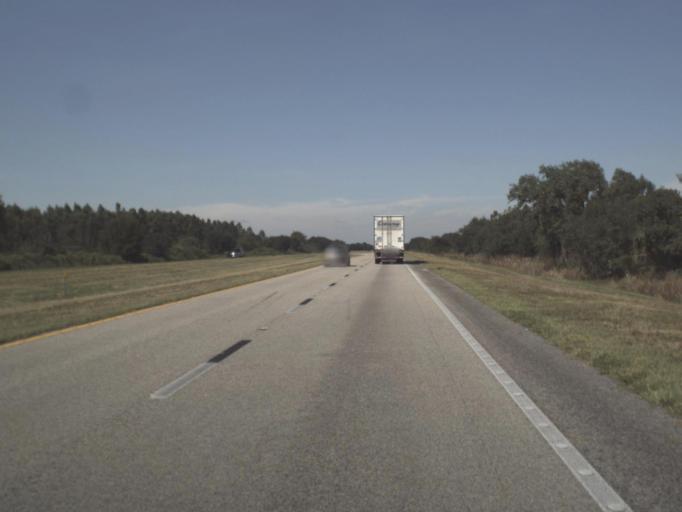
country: US
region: Florida
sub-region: Highlands County
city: Placid Lakes
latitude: 27.0108
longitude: -81.3340
